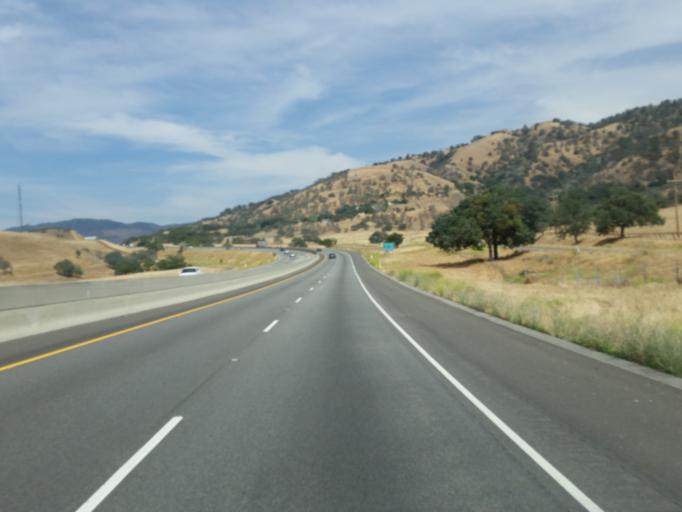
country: US
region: California
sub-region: Kern County
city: Bear Valley Springs
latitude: 35.2637
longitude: -118.6455
